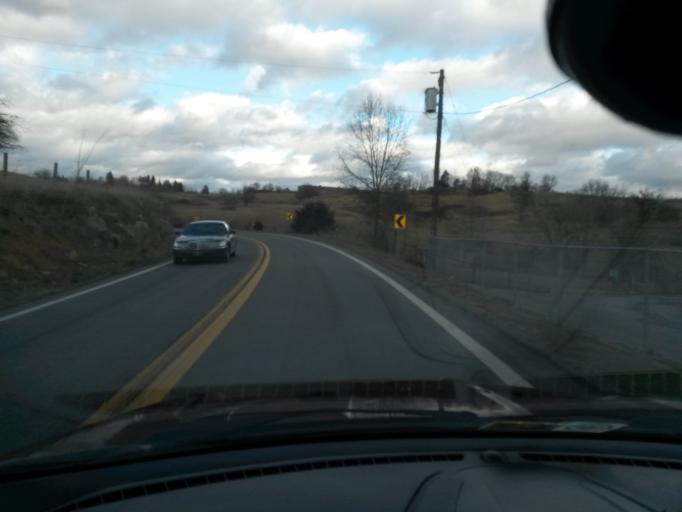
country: US
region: West Virginia
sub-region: Monroe County
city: Union
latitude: 37.5813
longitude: -80.5492
